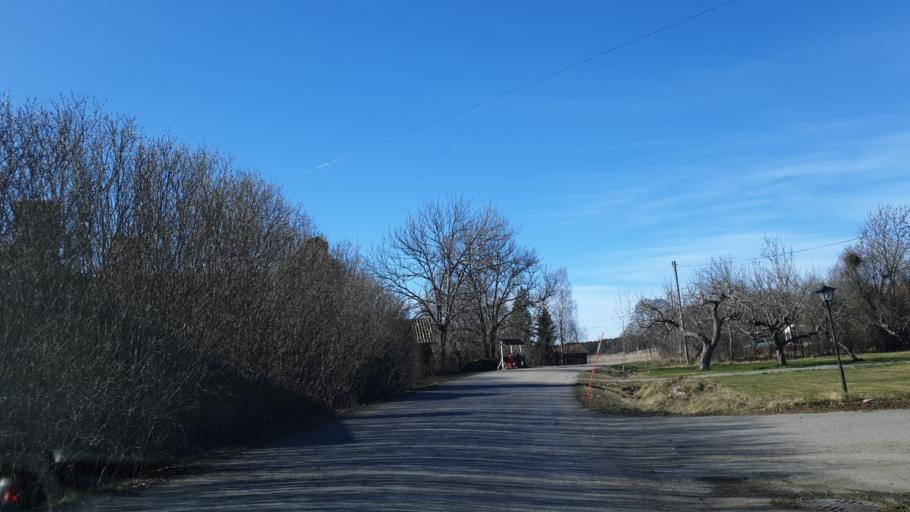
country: SE
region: Uppsala
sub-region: Enkopings Kommun
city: Dalby
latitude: 59.5211
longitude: 17.2763
